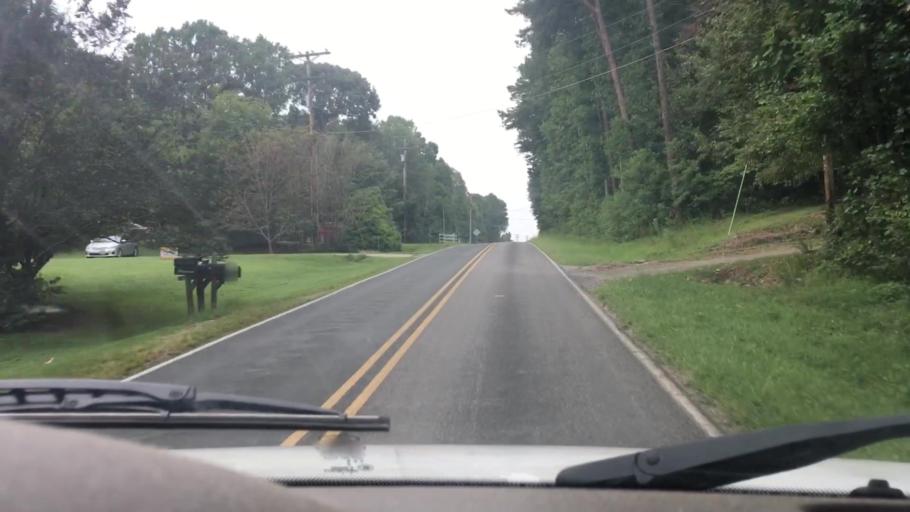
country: US
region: North Carolina
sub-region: Gaston County
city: Davidson
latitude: 35.5185
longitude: -80.8188
